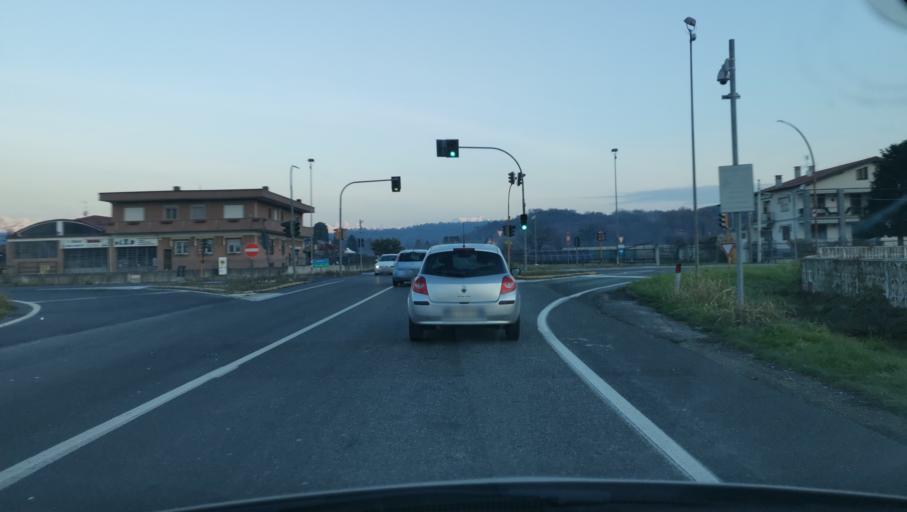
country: IT
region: Piedmont
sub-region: Provincia di Torino
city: Caluso
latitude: 45.3078
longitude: 7.8788
